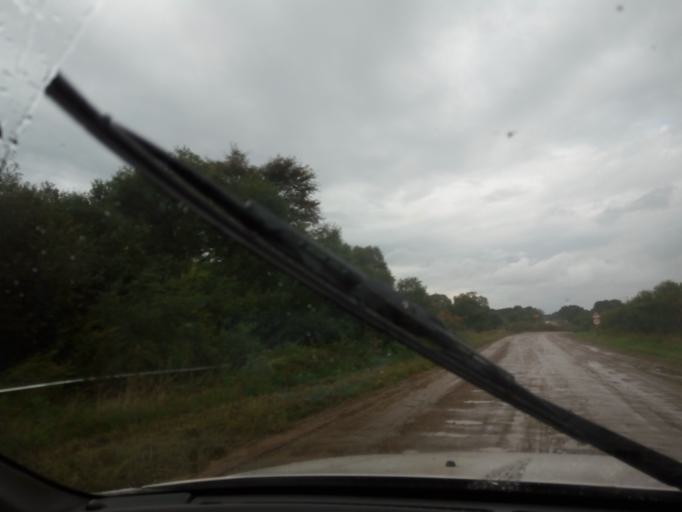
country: RU
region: Primorskiy
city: Lazo
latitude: 45.8516
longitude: 133.6460
